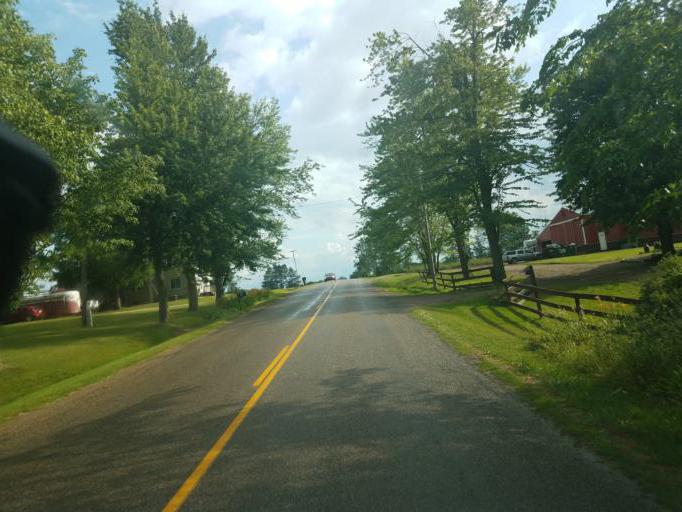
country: US
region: Michigan
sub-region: Eaton County
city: Bellevue
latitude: 42.5073
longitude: -85.0161
